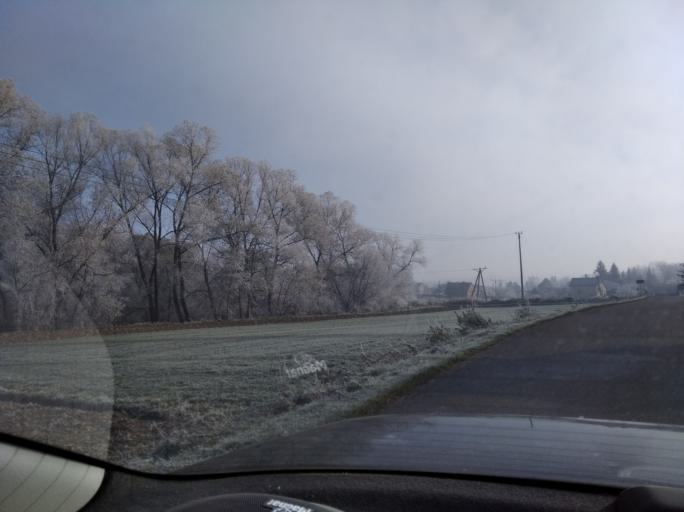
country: PL
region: Subcarpathian Voivodeship
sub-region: Powiat strzyzowski
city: Strzyzow
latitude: 49.8623
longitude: 21.7743
